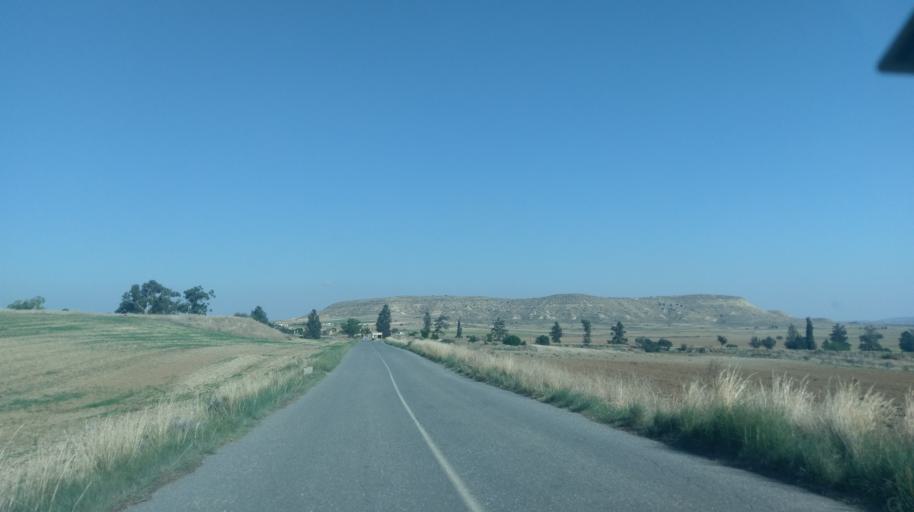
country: CY
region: Larnaka
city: Athienou
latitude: 35.0724
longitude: 33.4879
